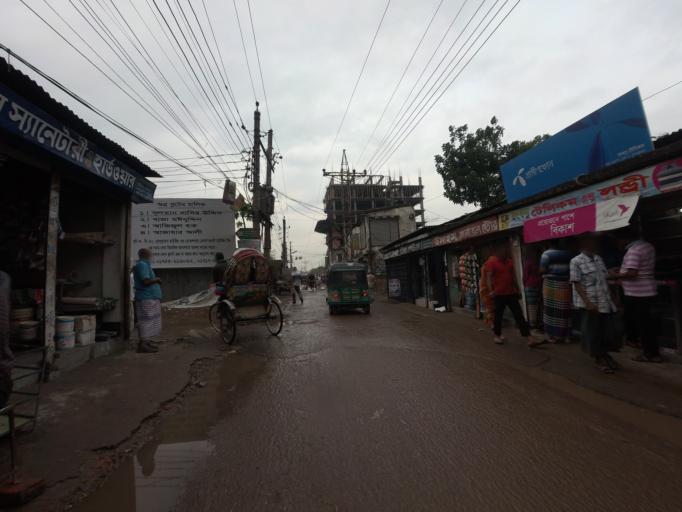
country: BD
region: Dhaka
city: Azimpur
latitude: 23.7762
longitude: 90.3523
